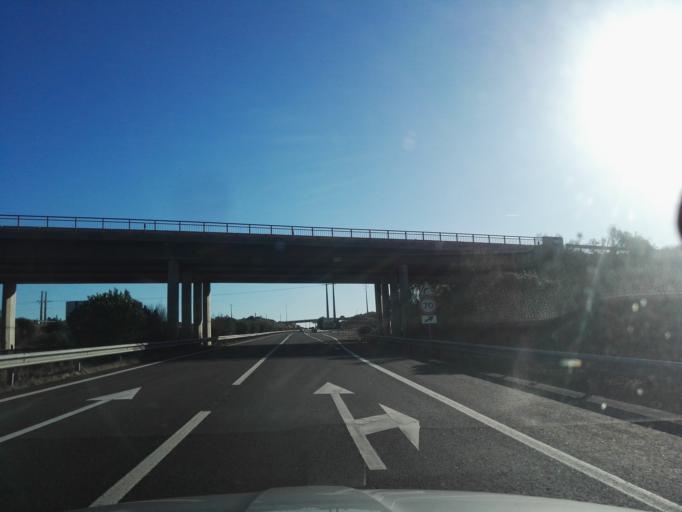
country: PT
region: Santarem
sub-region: Alcanena
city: Alcanena
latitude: 39.4797
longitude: -8.6229
